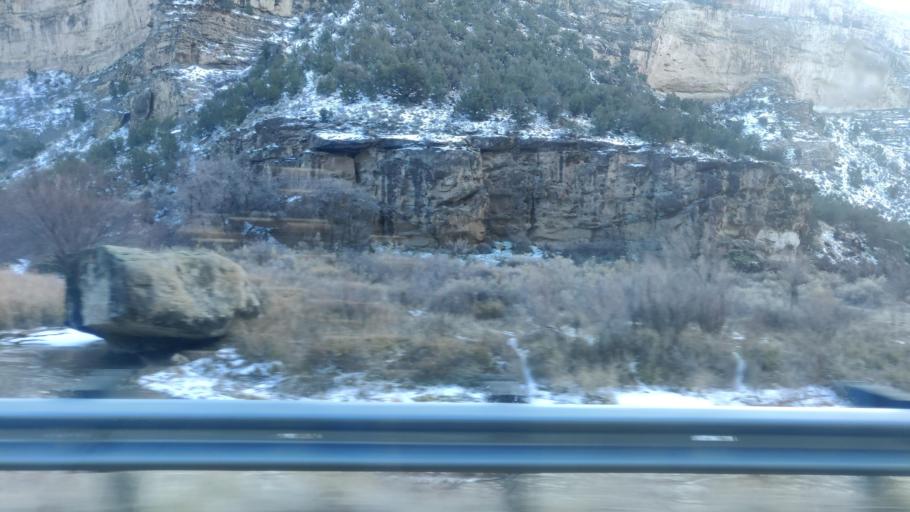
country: US
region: Colorado
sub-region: Mesa County
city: Palisade
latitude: 39.1912
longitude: -108.2444
